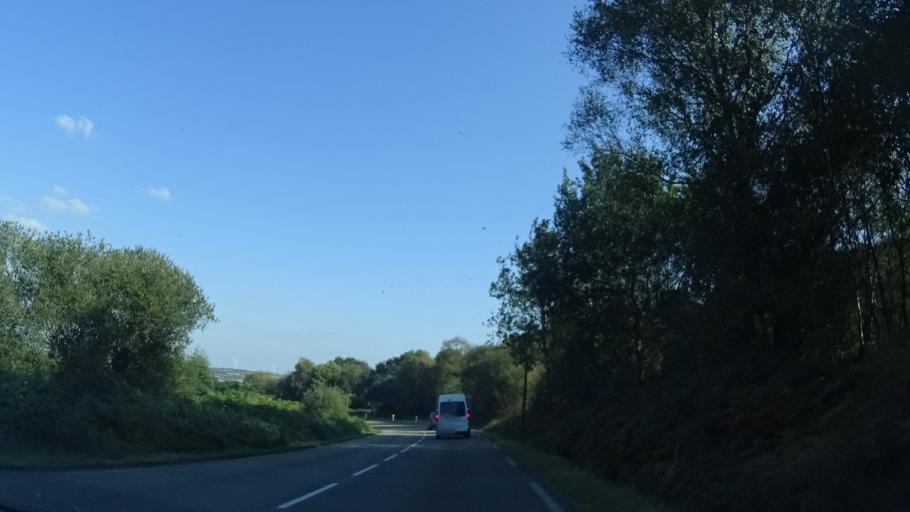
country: FR
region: Brittany
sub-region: Departement du Finistere
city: Cast
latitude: 48.1769
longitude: -4.1170
